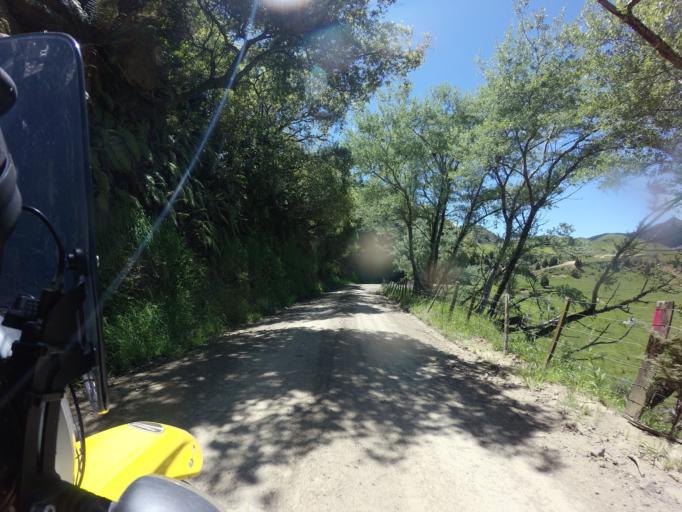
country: NZ
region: Bay of Plenty
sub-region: Opotiki District
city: Opotiki
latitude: -38.3935
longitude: 177.4590
